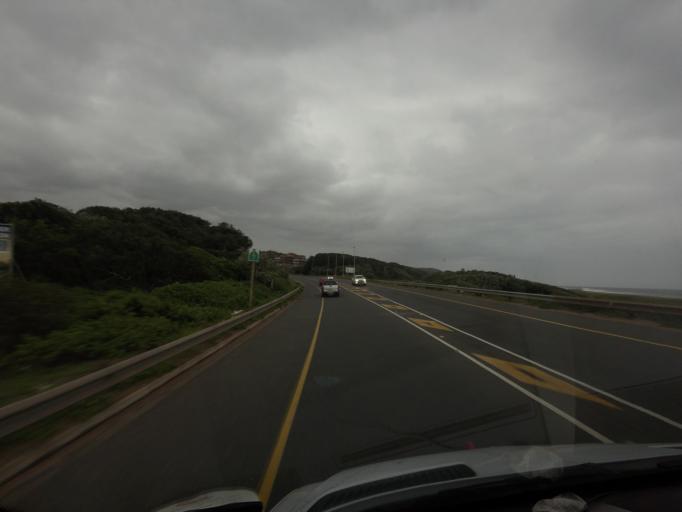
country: ZA
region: KwaZulu-Natal
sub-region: iLembe District Municipality
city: Ballitoville
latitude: -29.5707
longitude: 31.1855
